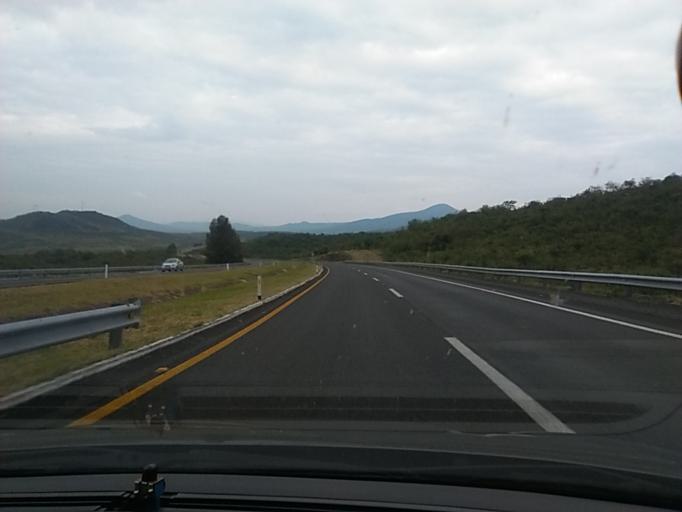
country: MX
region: Michoacan
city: Panindicuaro de la Reforma
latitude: 19.9965
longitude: -101.8292
